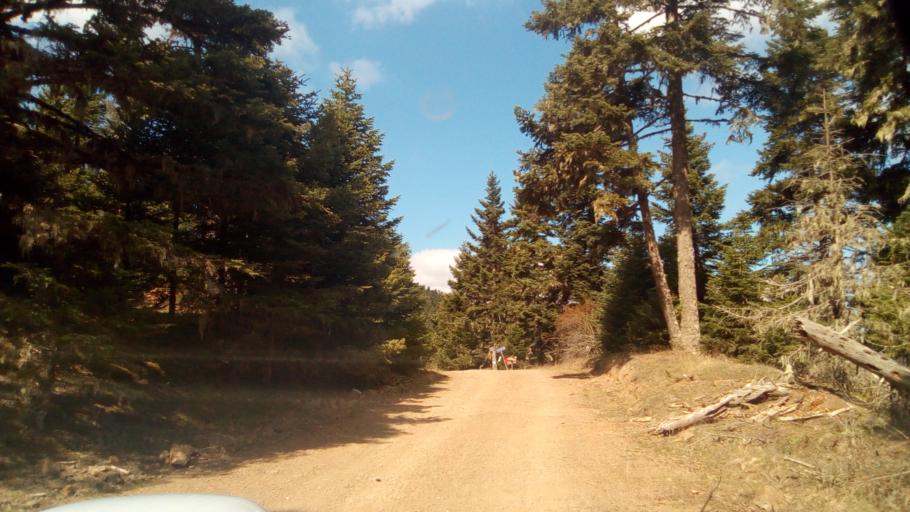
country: GR
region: West Greece
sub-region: Nomos Aitolias kai Akarnanias
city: Nafpaktos
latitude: 38.6395
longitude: 21.9418
